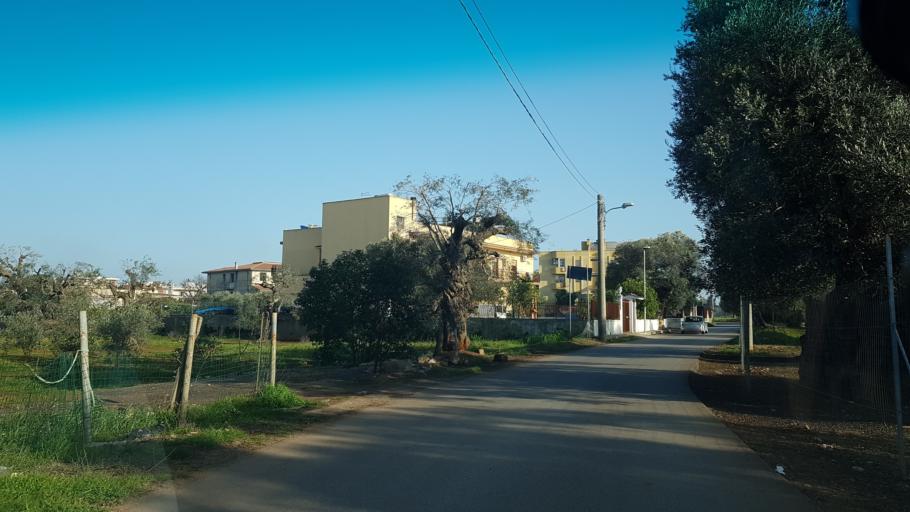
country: IT
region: Apulia
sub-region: Provincia di Brindisi
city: San Vito dei Normanni
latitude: 40.6649
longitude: 17.6926
